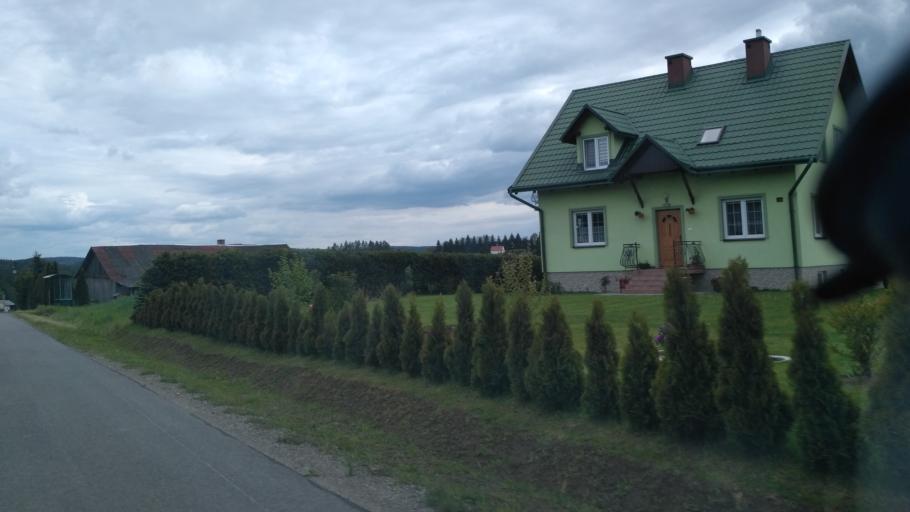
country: PL
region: Subcarpathian Voivodeship
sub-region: Powiat przemyski
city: Przedmiescie Dubieckie
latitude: 49.8336
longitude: 22.3219
